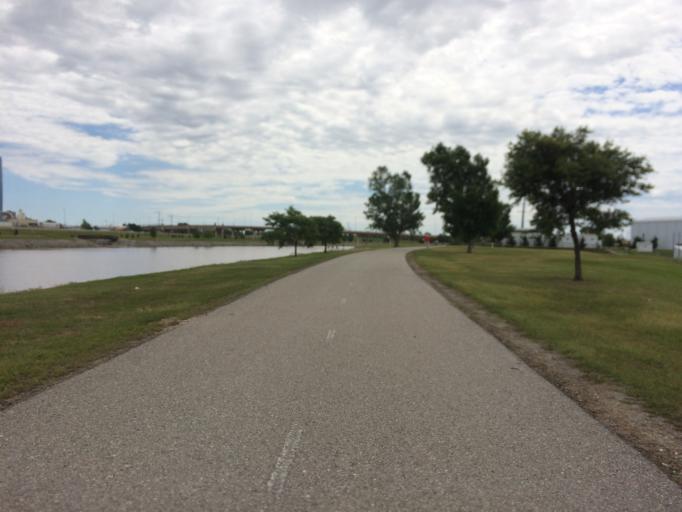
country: US
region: Oklahoma
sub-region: Oklahoma County
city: Oklahoma City
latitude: 35.4593
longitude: -97.5430
